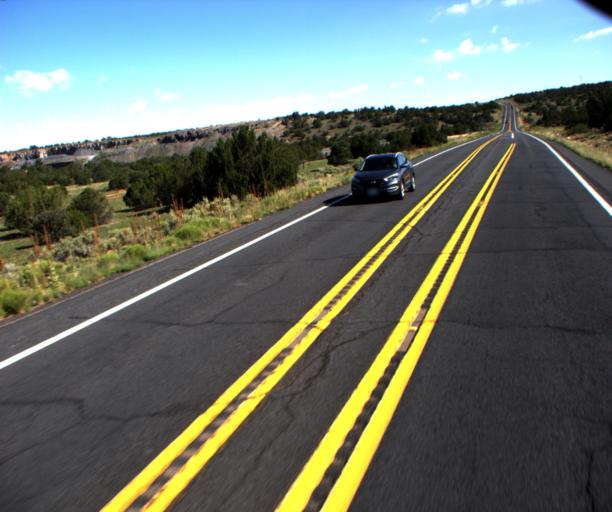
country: US
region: Arizona
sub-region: Coconino County
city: Williams
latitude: 35.4806
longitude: -112.1767
